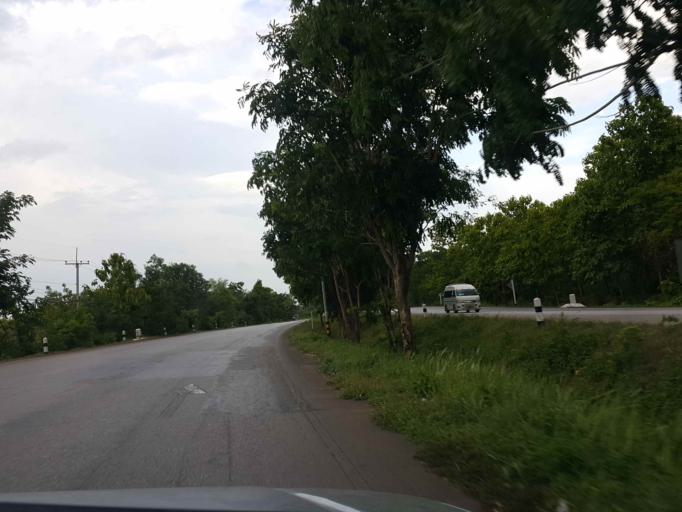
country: TH
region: Lampang
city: Soem Ngam
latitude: 18.0130
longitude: 99.3580
